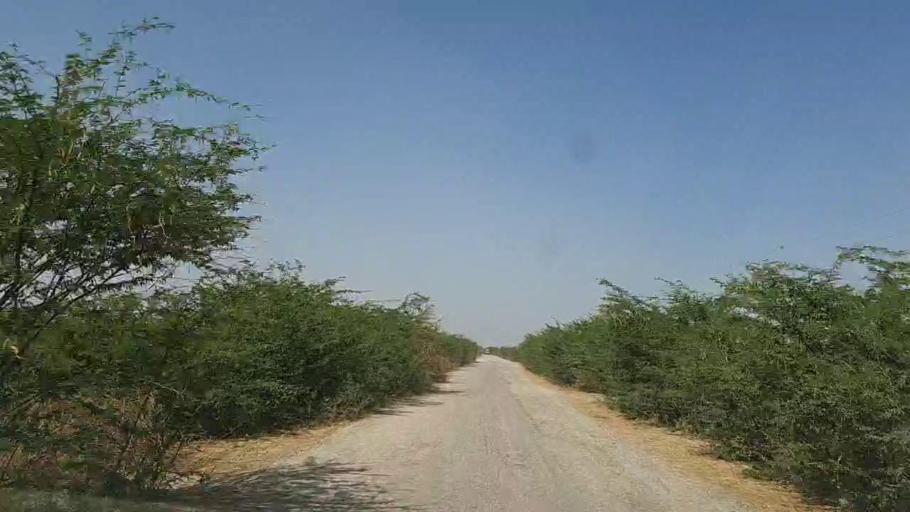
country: PK
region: Sindh
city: Naukot
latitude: 24.6347
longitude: 69.2882
